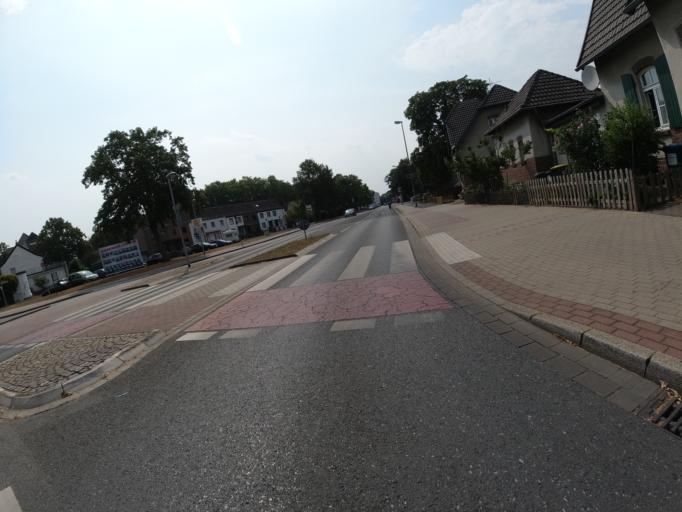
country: DE
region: North Rhine-Westphalia
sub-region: Regierungsbezirk Dusseldorf
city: Moers
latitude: 51.4524
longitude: 6.6466
